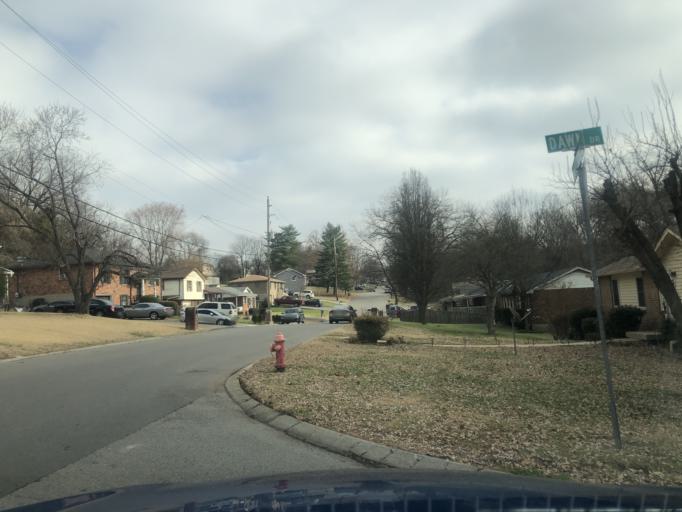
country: US
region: Tennessee
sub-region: Davidson County
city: Oak Hill
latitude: 36.0903
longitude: -86.7134
